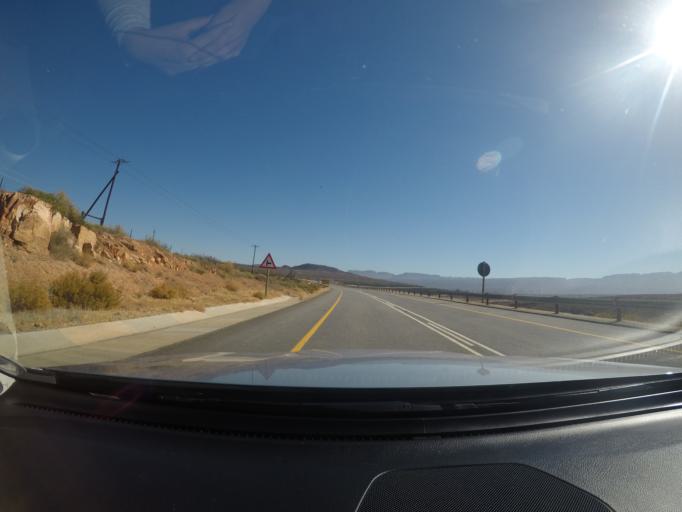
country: ZA
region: Western Cape
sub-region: West Coast District Municipality
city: Clanwilliam
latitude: -32.2146
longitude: 18.8575
